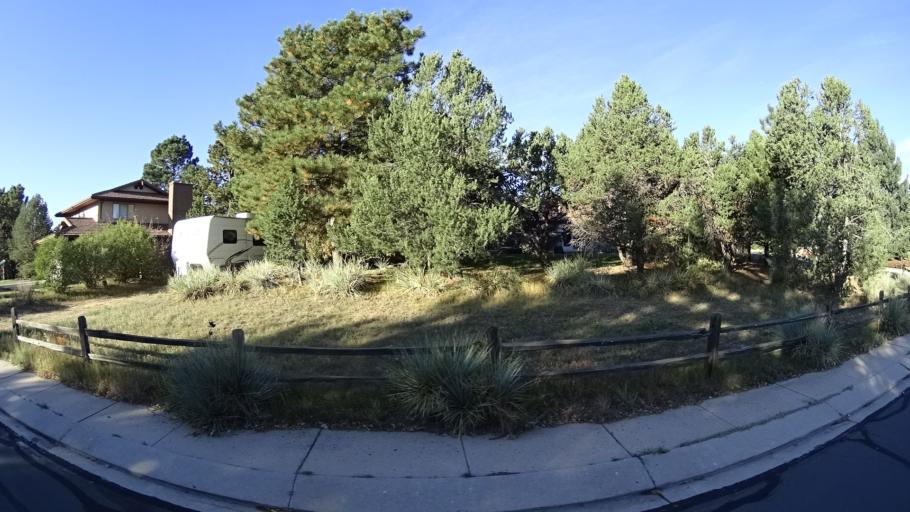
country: US
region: Colorado
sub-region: El Paso County
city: Cimarron Hills
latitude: 38.8838
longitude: -104.7655
